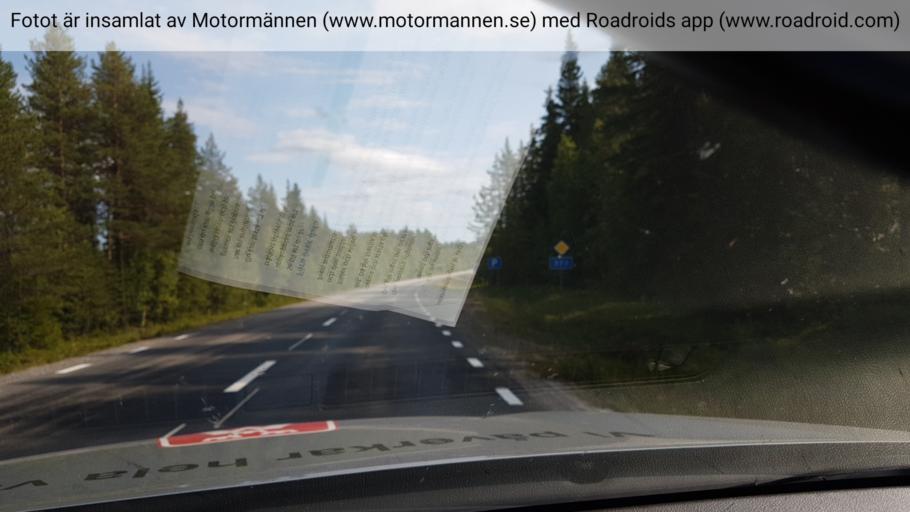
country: SE
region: Vaesterbotten
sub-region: Skelleftea Kommun
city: Storvik
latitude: 65.3837
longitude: 20.3410
